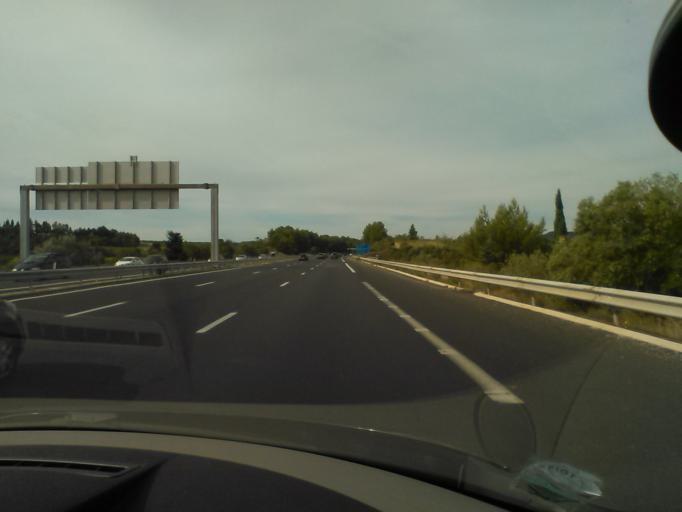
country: FR
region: Languedoc-Roussillon
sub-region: Departement du Gard
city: Remoulins
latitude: 43.9319
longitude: 4.5968
